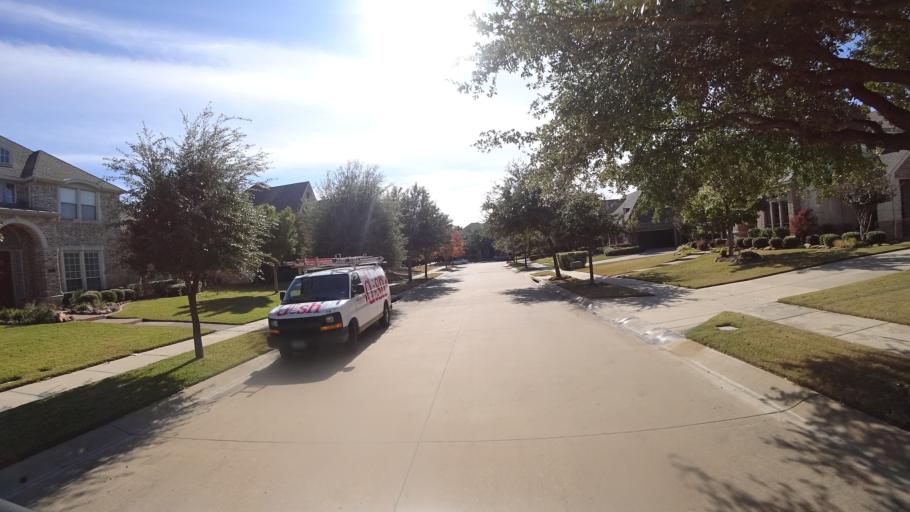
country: US
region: Texas
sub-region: Denton County
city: The Colony
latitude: 33.0353
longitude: -96.8923
